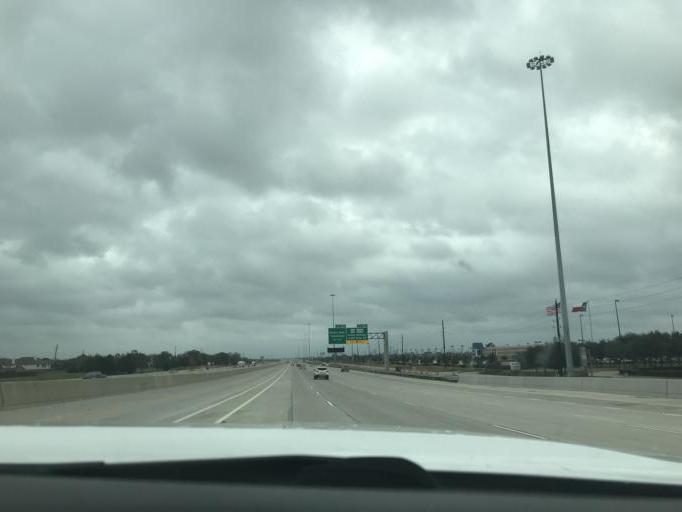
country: US
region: Texas
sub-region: Fort Bend County
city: Greatwood
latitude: 29.5564
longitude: -95.7140
